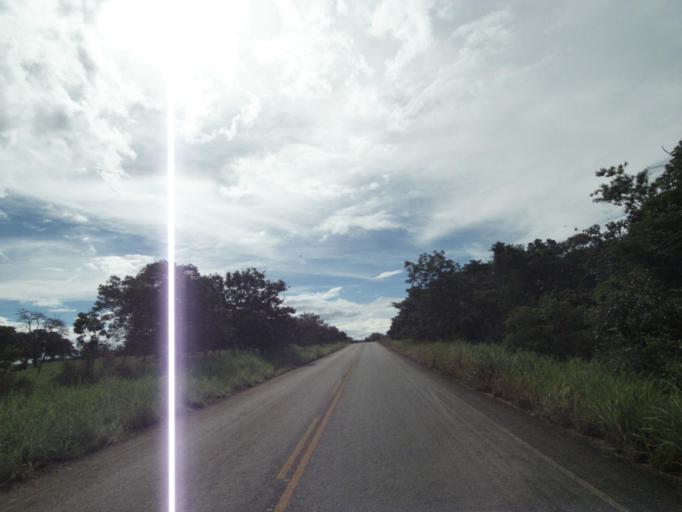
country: BR
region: Goias
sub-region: Pirenopolis
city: Pirenopolis
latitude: -15.7834
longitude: -49.0425
